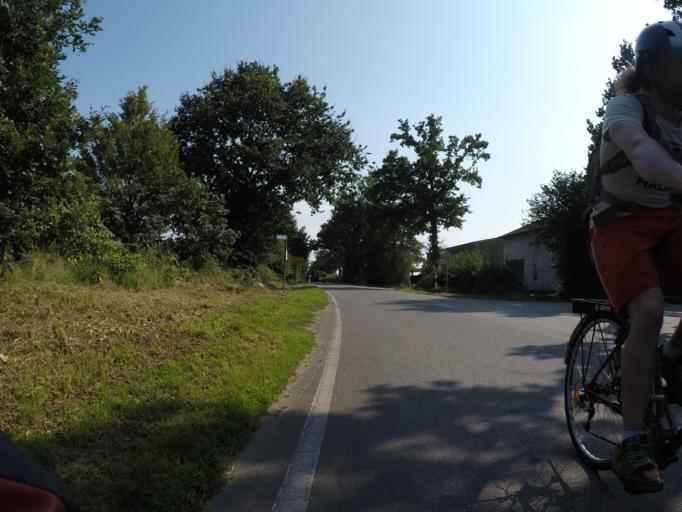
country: DE
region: Schleswig-Holstein
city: Todesfelde
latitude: 53.8895
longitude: 10.1774
